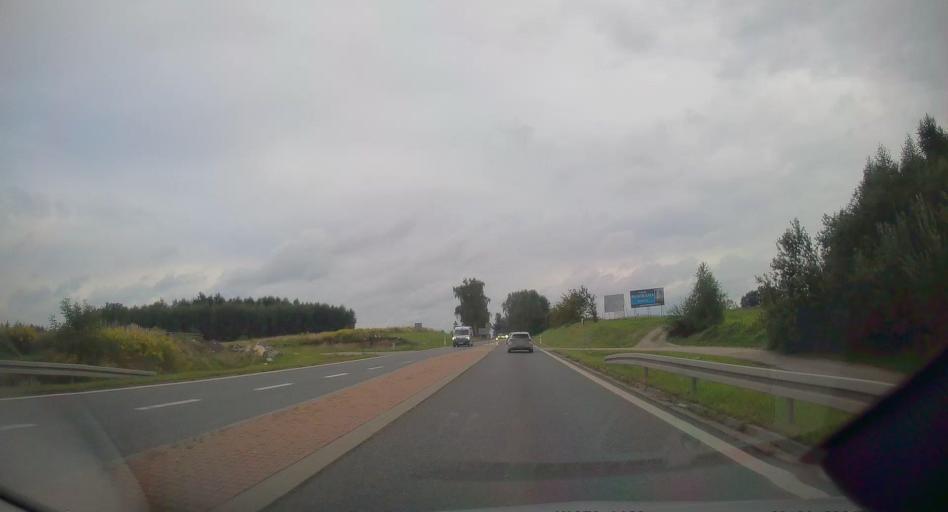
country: PL
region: Lesser Poland Voivodeship
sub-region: Powiat wielicki
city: Targowisko
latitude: 49.9862
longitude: 20.2834
